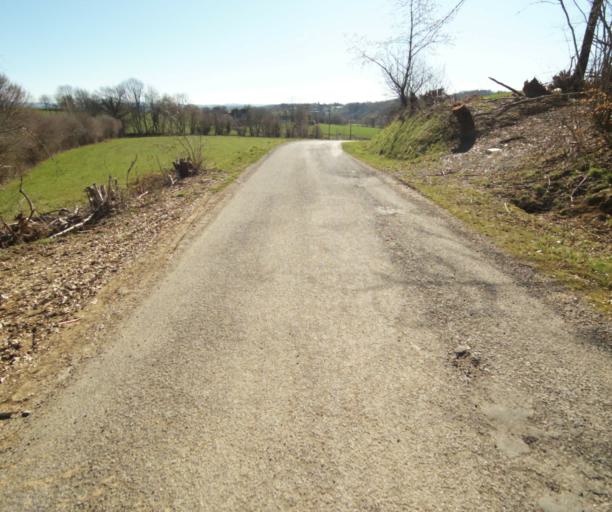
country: FR
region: Limousin
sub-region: Departement de la Correze
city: Chamboulive
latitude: 45.4042
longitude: 1.7082
